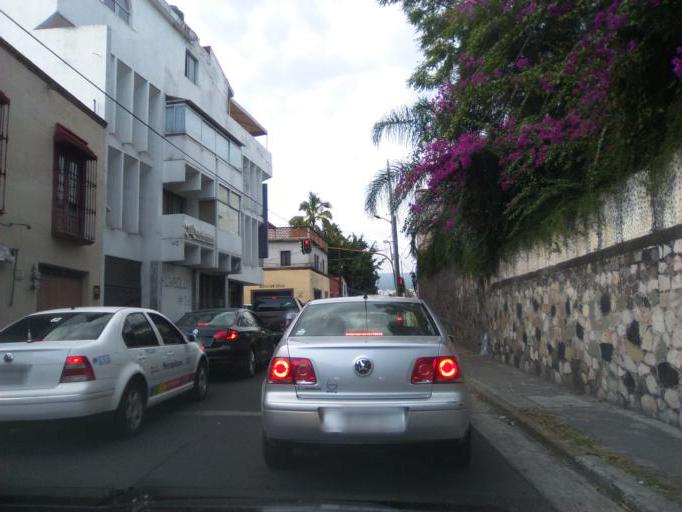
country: MX
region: Morelos
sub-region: Cuernavaca
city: Cuernavaca
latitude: 18.9182
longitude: -99.2308
